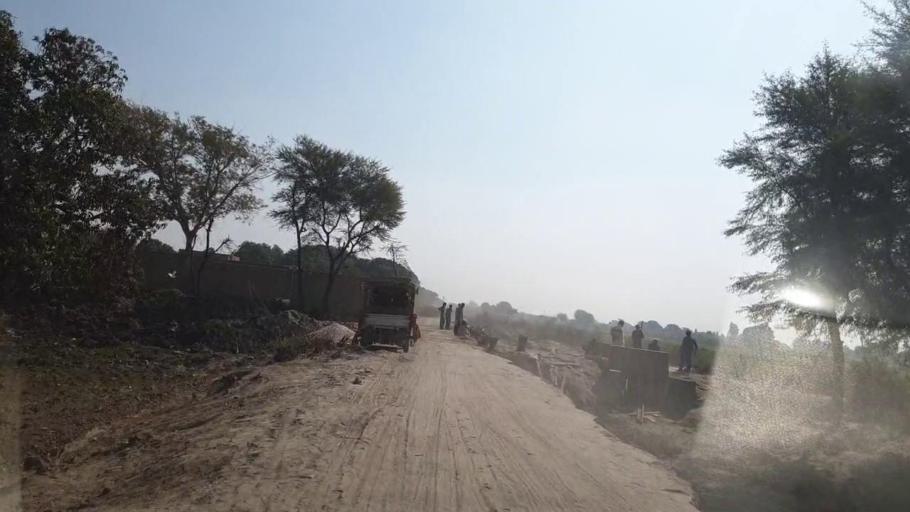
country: PK
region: Sindh
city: Matiari
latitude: 25.5122
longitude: 68.4610
